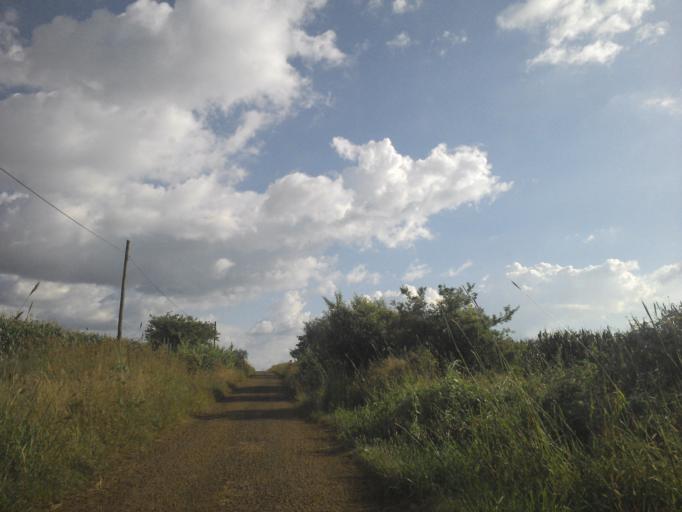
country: MX
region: Jalisco
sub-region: Atotonilco el Alto
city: Ojo de Agua de Moran
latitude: 20.6068
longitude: -102.4708
